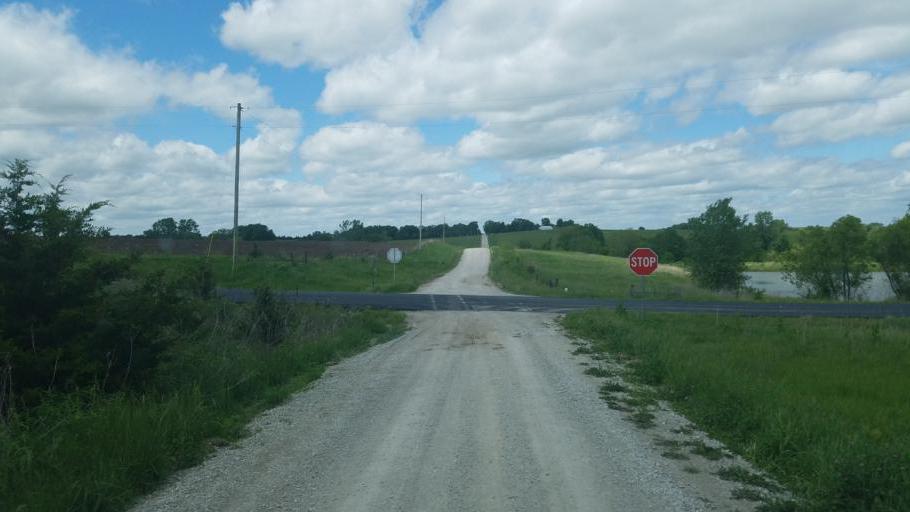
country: US
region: Iowa
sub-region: Decatur County
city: Lamoni
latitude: 40.5147
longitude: -94.0228
